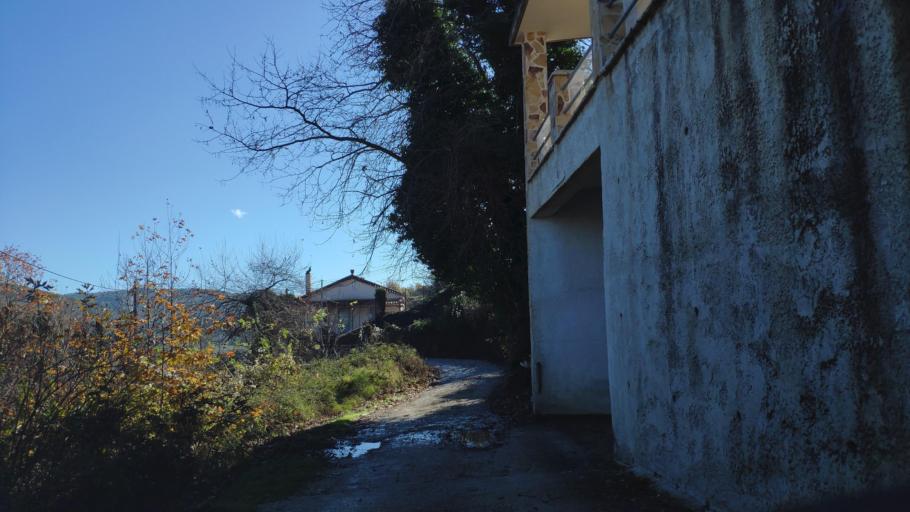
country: GR
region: West Greece
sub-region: Nomos Achaias
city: Aiyira
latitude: 38.0638
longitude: 22.4547
